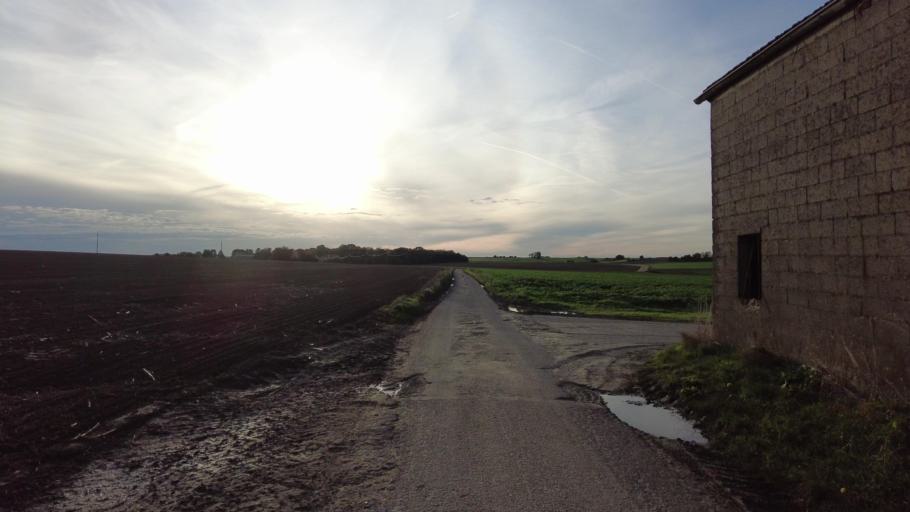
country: BE
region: Flanders
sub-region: Provincie Vlaams-Brabant
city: Tienen
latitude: 50.7471
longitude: 4.9452
